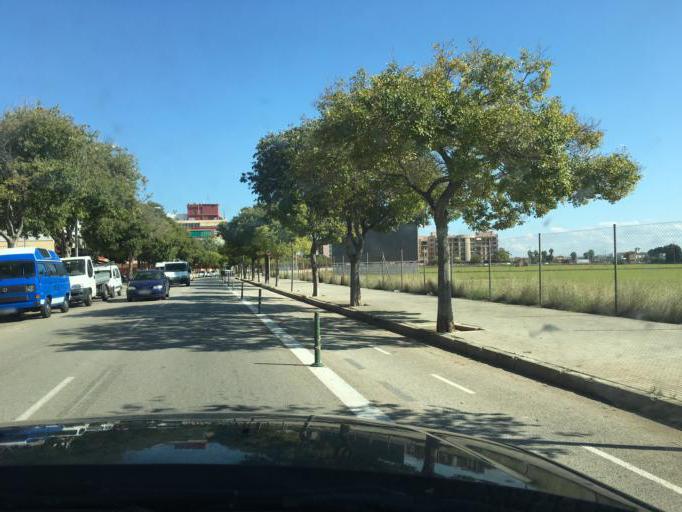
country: ES
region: Balearic Islands
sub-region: Illes Balears
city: Palma
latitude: 39.5814
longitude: 2.6788
